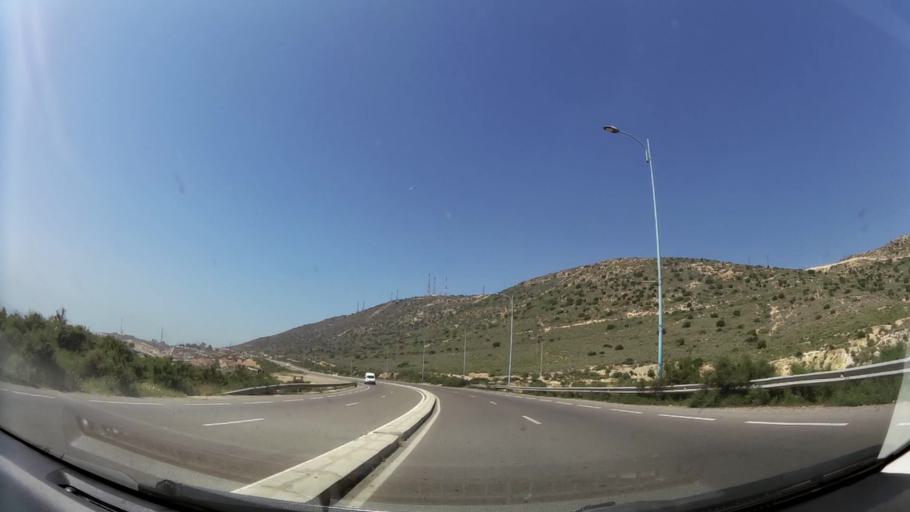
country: MA
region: Souss-Massa-Draa
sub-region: Agadir-Ida-ou-Tnan
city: Agadir
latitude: 30.4290
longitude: -9.6313
